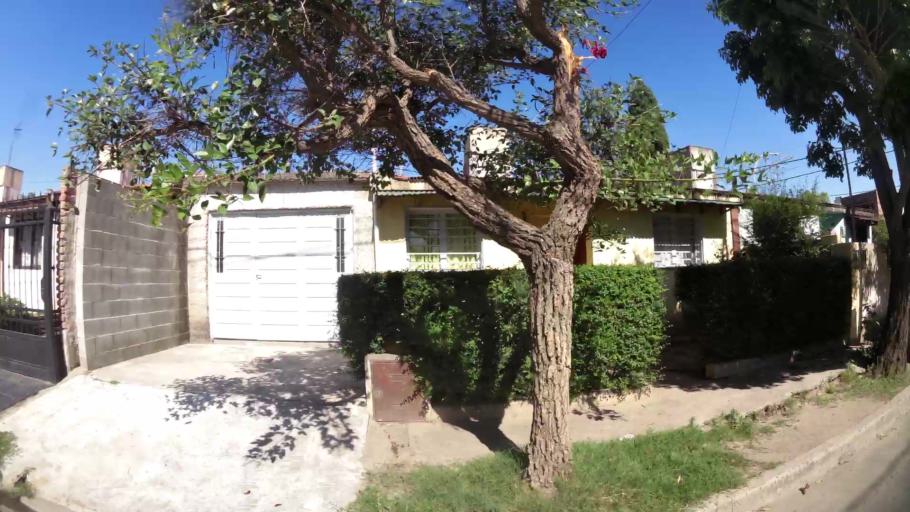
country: AR
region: Cordoba
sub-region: Departamento de Capital
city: Cordoba
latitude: -31.4433
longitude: -64.1385
